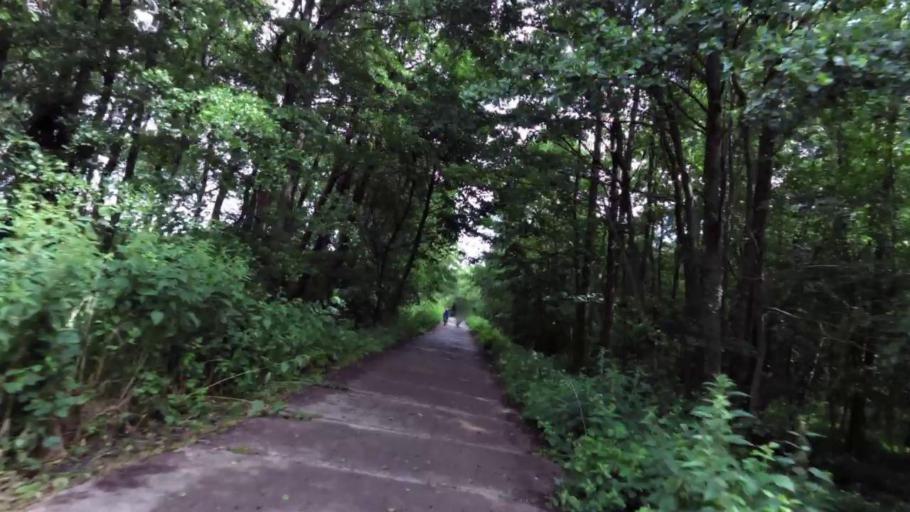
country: PL
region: West Pomeranian Voivodeship
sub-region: Powiat slawienski
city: Darlowo
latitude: 54.4912
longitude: 16.4404
